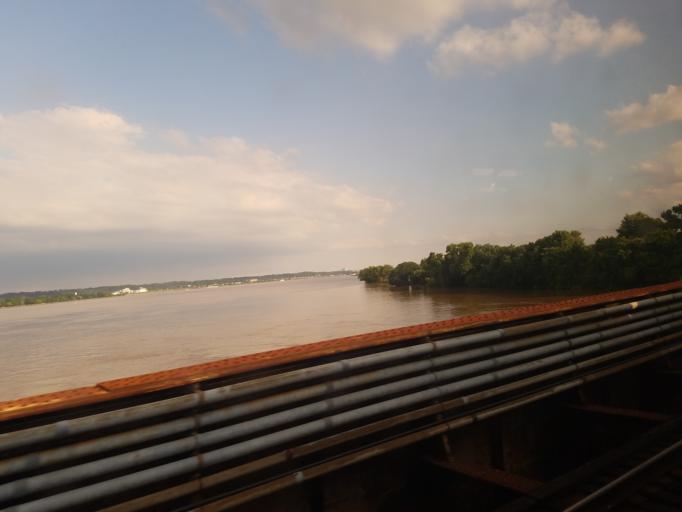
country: US
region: Washington, D.C.
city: Washington, D.C.
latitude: 38.8726
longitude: -77.0402
